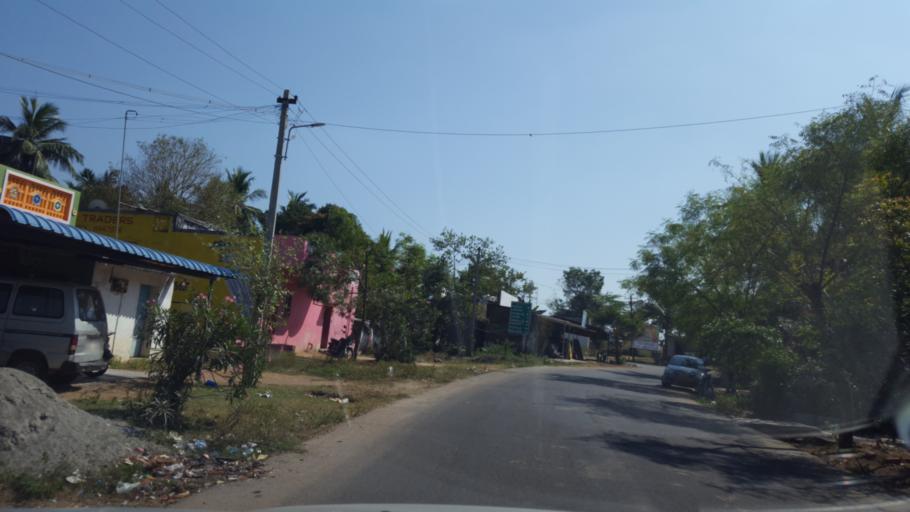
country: IN
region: Tamil Nadu
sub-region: Kancheepuram
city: Kanchipuram
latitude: 12.8367
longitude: 79.7393
